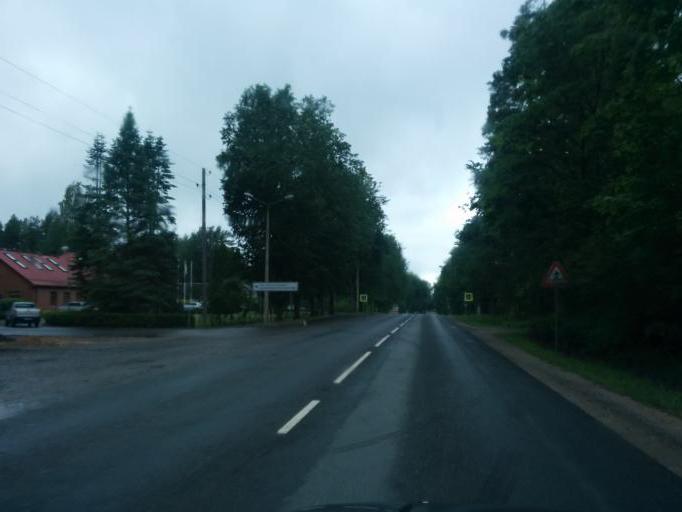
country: LV
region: Smiltene
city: Smiltene
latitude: 57.4085
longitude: 25.9422
